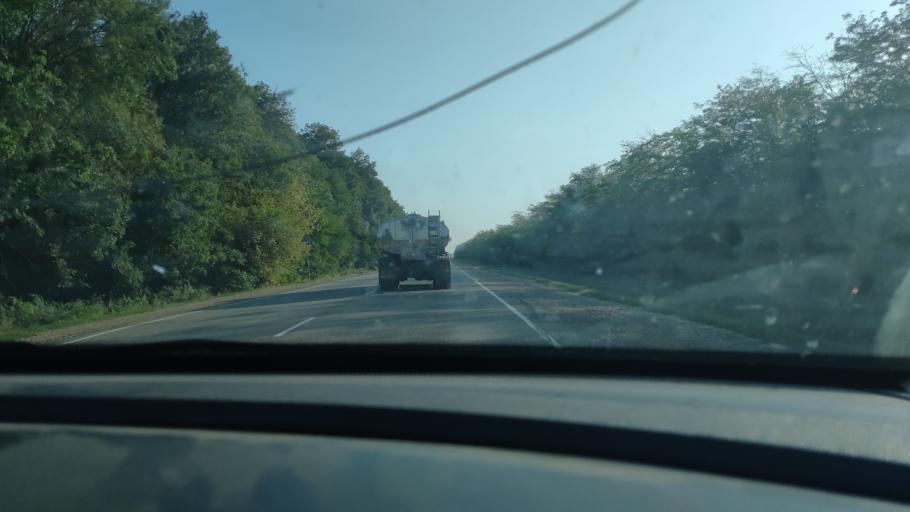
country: RU
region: Krasnodarskiy
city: Starominskaya
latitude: 46.4883
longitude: 39.0569
